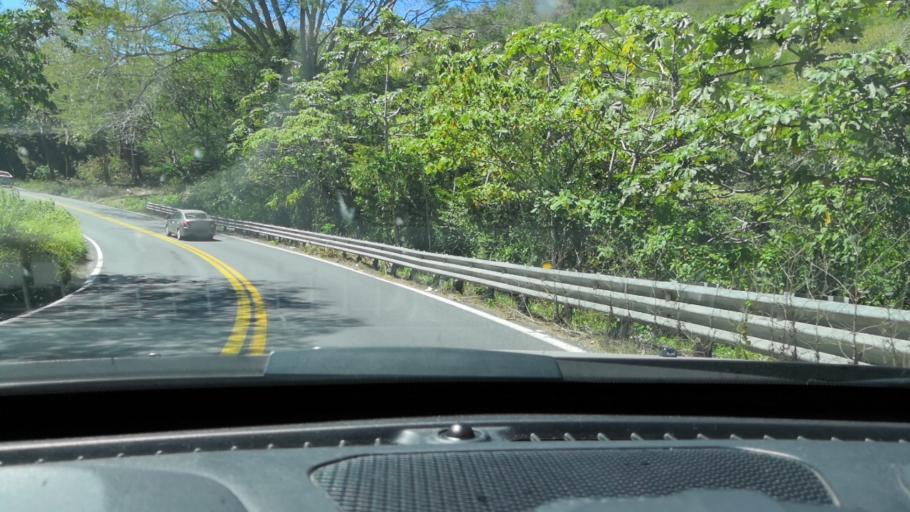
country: MX
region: Nayarit
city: Compostela
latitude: 21.2163
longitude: -104.9858
